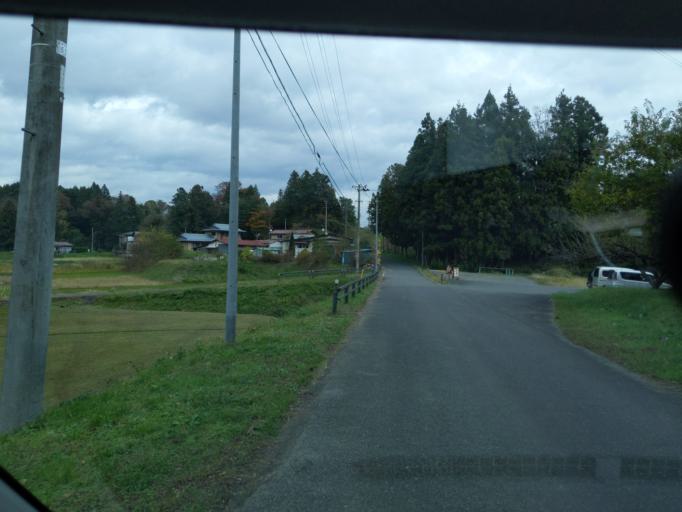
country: JP
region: Iwate
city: Ichinoseki
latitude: 39.0231
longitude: 141.1330
